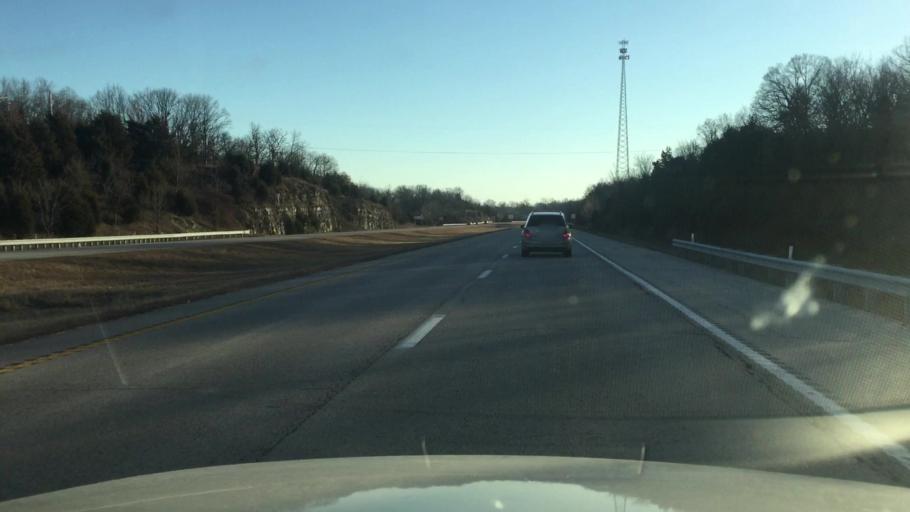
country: US
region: Missouri
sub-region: Cole County
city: Wardsville
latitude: 38.4828
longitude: -92.2727
